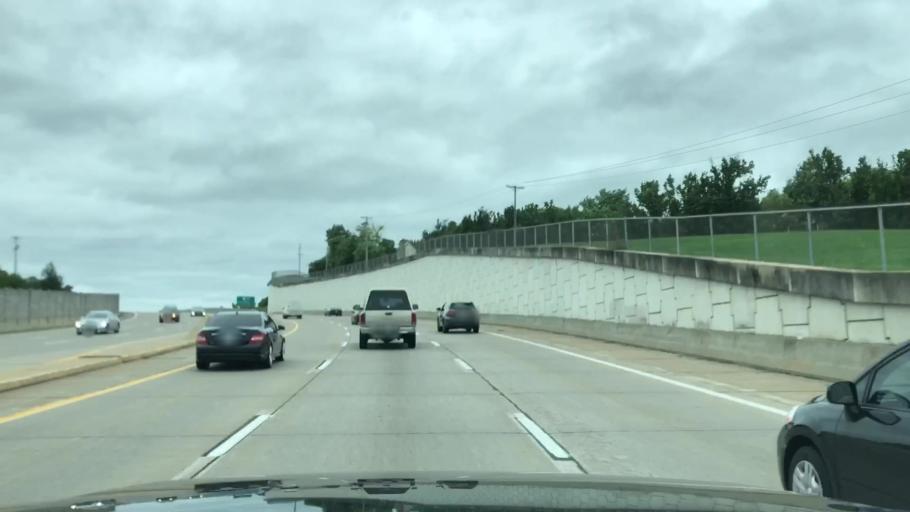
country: US
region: Missouri
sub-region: Saint Louis County
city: Manchester
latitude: 38.6041
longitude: -90.5105
